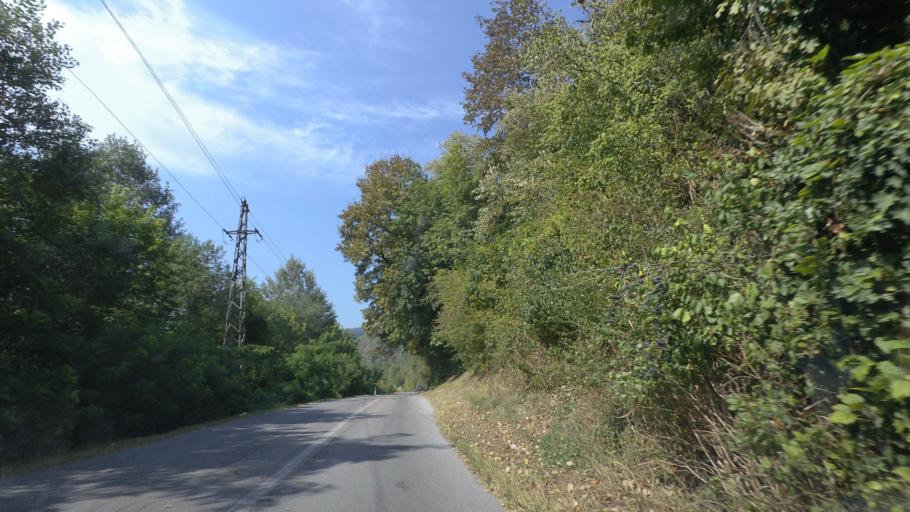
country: BA
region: Republika Srpska
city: Kostajnica
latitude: 45.2156
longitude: 16.4997
